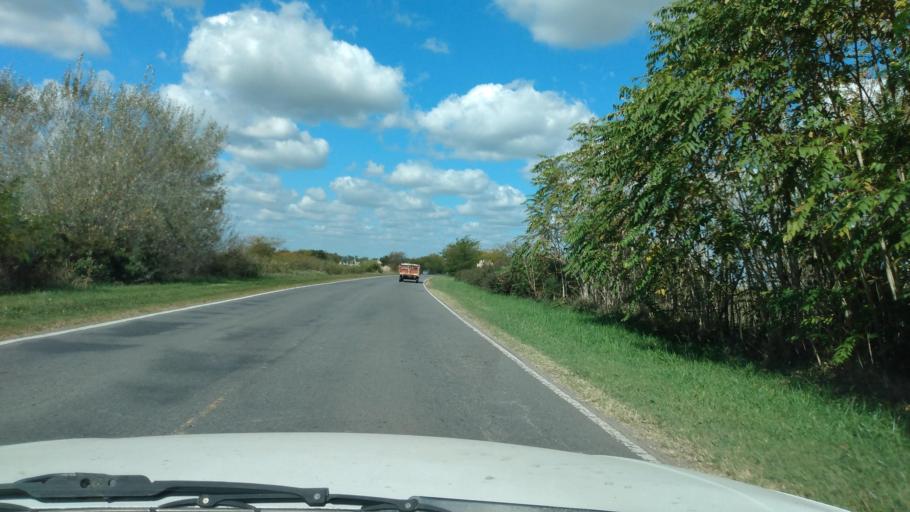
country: AR
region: Buenos Aires
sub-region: Partido de Navarro
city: Navarro
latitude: -34.9390
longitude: -59.3217
